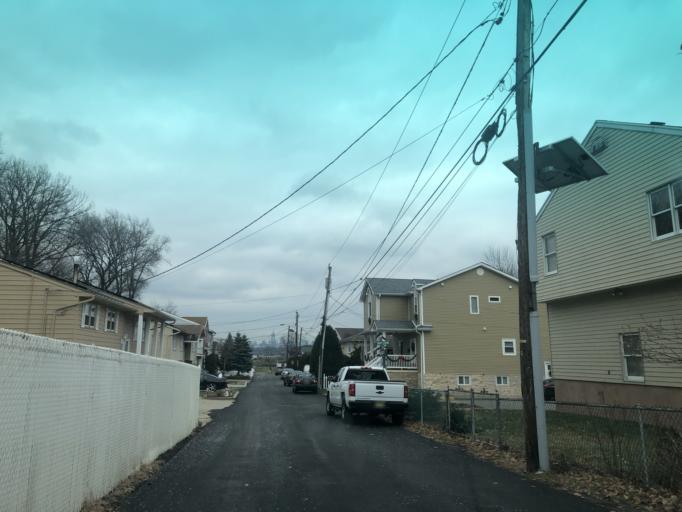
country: US
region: New Jersey
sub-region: Hudson County
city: Secaucus
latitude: 40.7989
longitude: -74.0519
